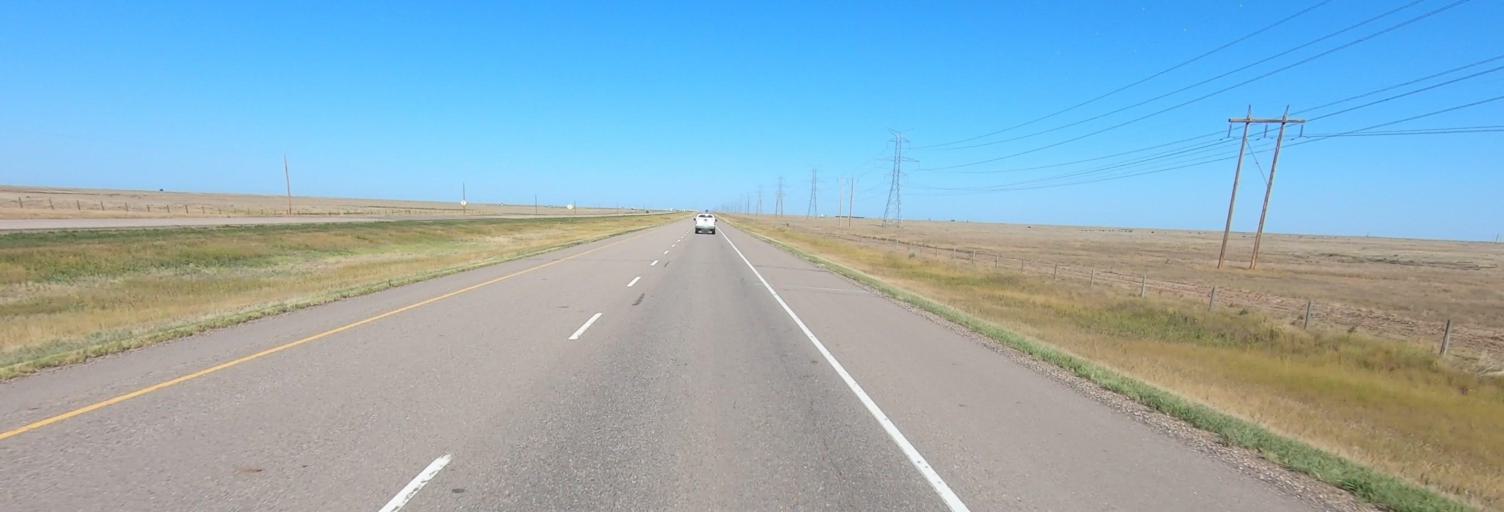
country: CA
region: Alberta
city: Brooks
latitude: 50.3913
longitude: -111.4717
